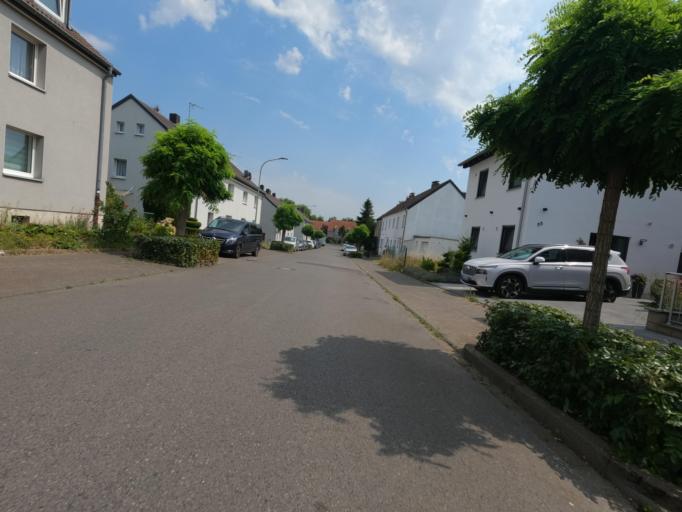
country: DE
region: North Rhine-Westphalia
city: Baesweiler
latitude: 50.9145
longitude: 6.1899
